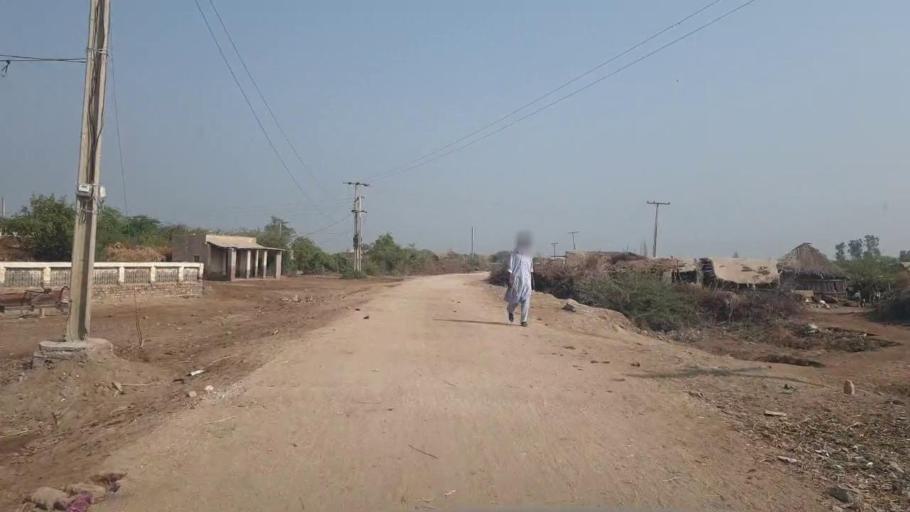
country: PK
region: Sindh
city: Umarkot
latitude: 25.3983
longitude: 69.6984
